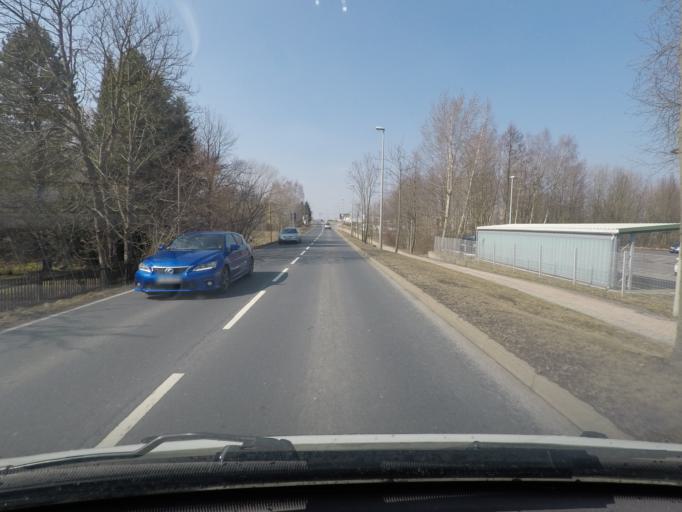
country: DE
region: Saxony
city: Freiberg
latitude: 50.9296
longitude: 13.3268
